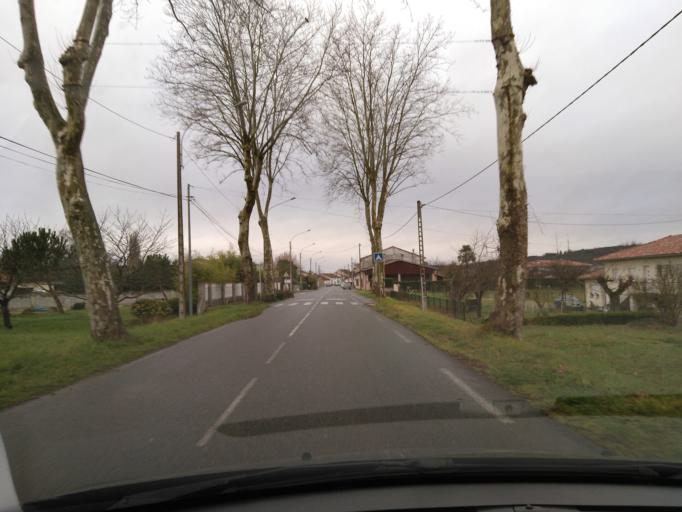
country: FR
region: Midi-Pyrenees
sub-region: Departement de la Haute-Garonne
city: Montesquieu-Volvestre
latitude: 43.2008
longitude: 1.2295
